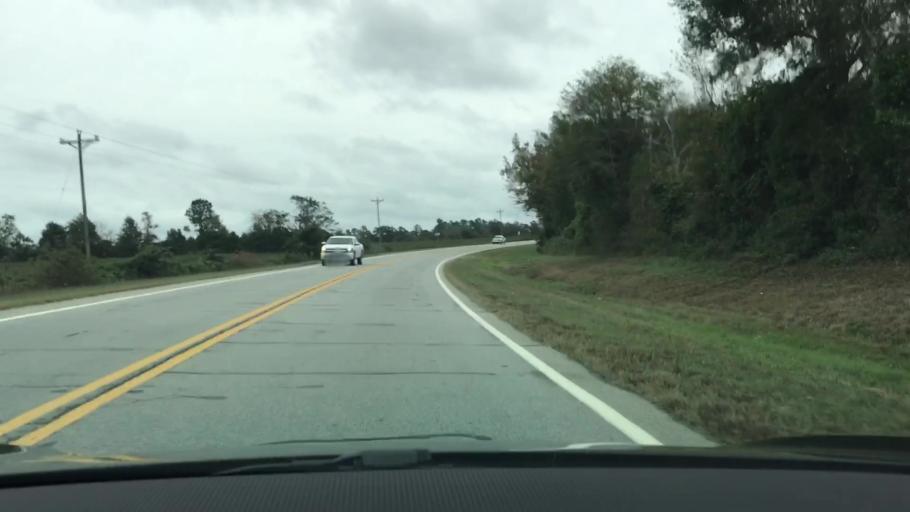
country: US
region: Georgia
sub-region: Glascock County
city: Gibson
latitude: 33.3309
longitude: -82.5618
